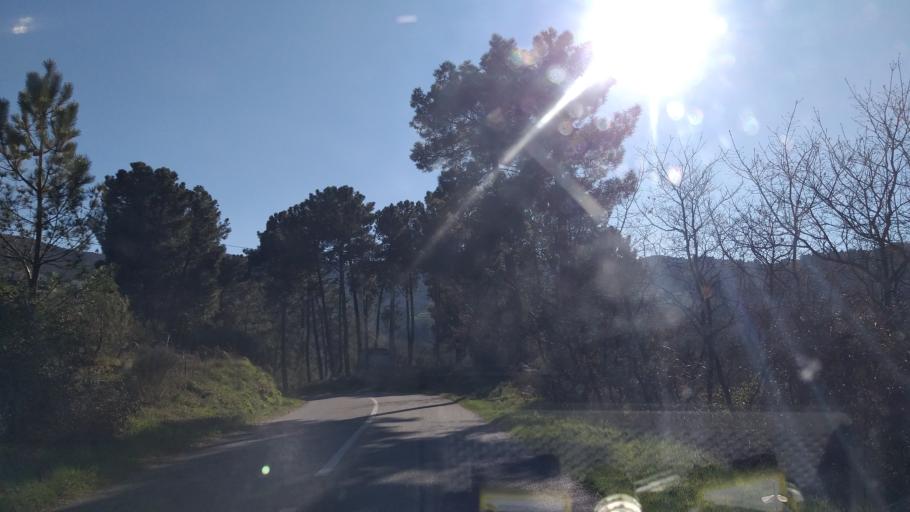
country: PT
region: Guarda
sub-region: Celorico da Beira
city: Celorico da Beira
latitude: 40.5909
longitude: -7.3603
